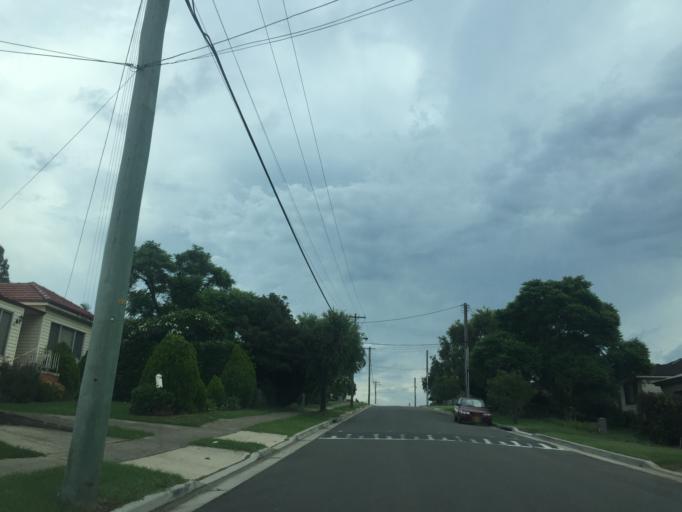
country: AU
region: New South Wales
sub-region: Blacktown
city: Blacktown
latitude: -33.7848
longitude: 150.8974
